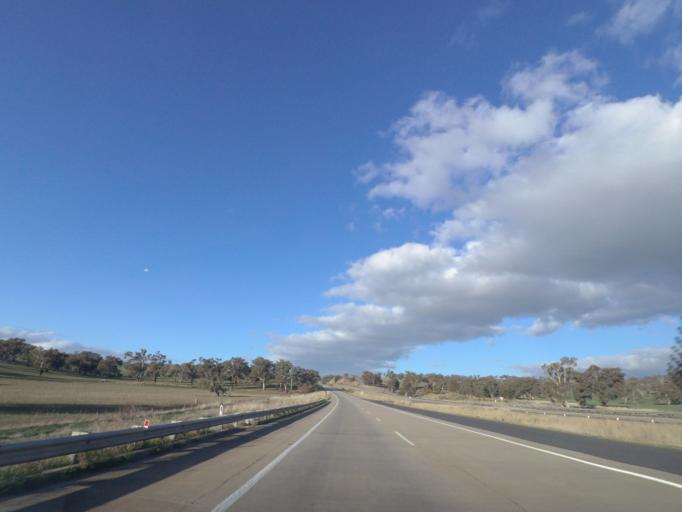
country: AU
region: New South Wales
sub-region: Gundagai
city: Gundagai
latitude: -34.8154
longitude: 148.4040
